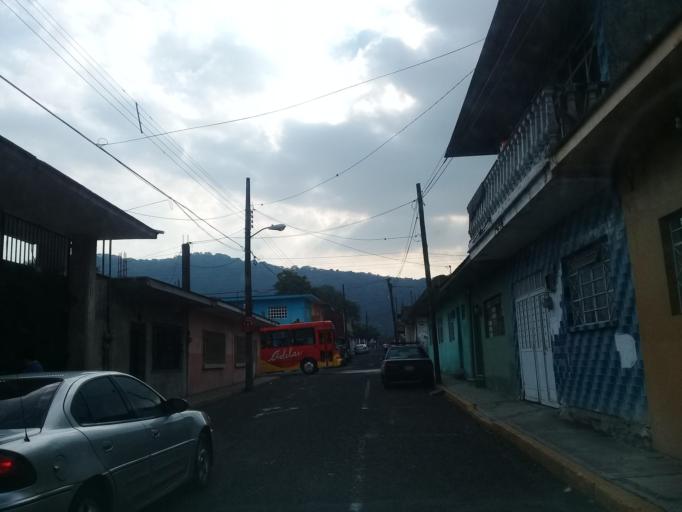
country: MX
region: Veracruz
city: Orizaba
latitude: 18.8590
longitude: -97.1065
